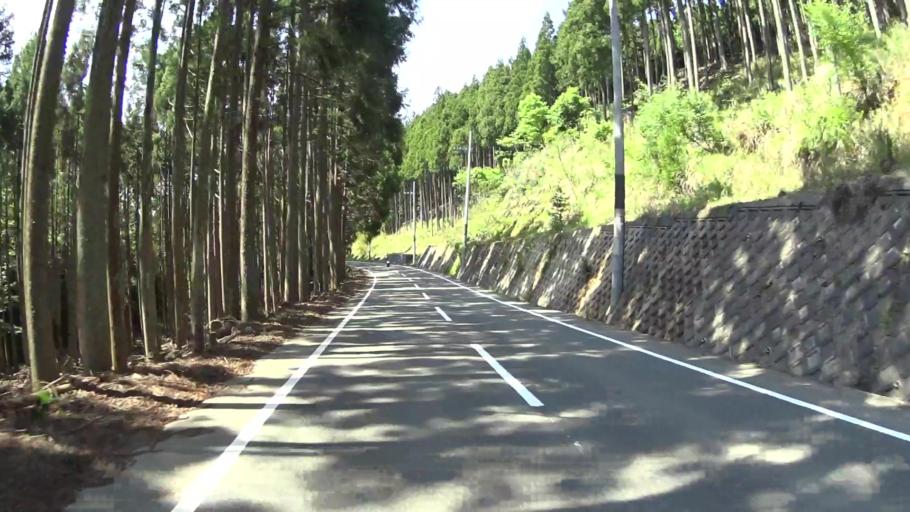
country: JP
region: Kyoto
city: Kameoka
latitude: 35.1144
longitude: 135.5681
